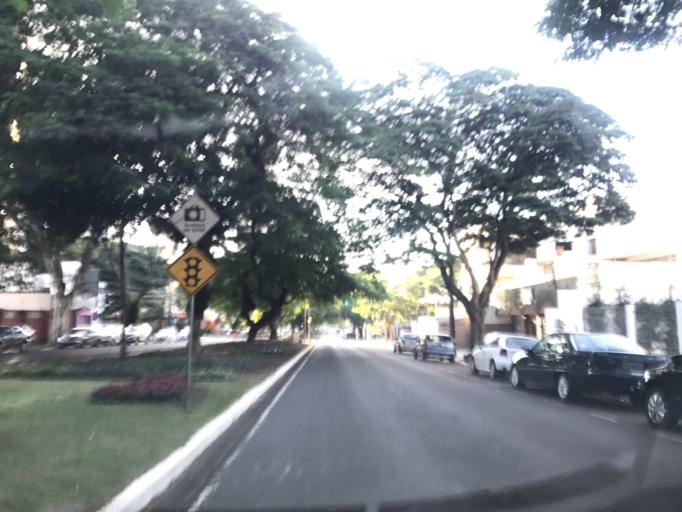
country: BR
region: Parana
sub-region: Maringa
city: Maringa
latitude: -23.4256
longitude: -51.9464
